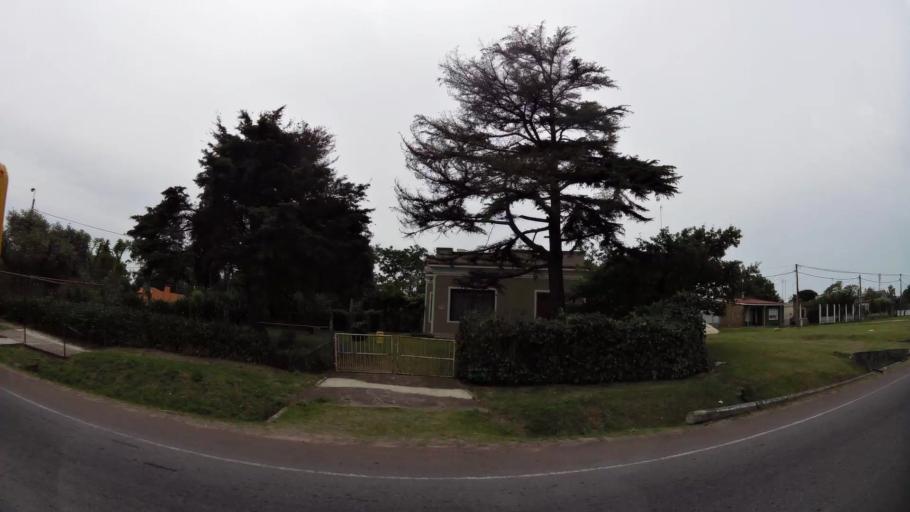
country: UY
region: Canelones
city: La Paz
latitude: -34.7719
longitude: -56.2267
